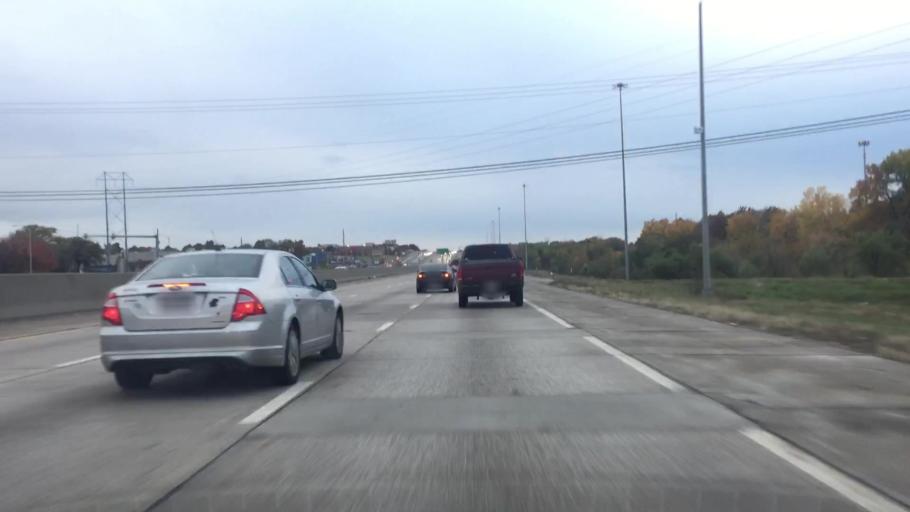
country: US
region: Kansas
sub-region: Johnson County
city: Overland Park
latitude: 38.9909
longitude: -94.6991
